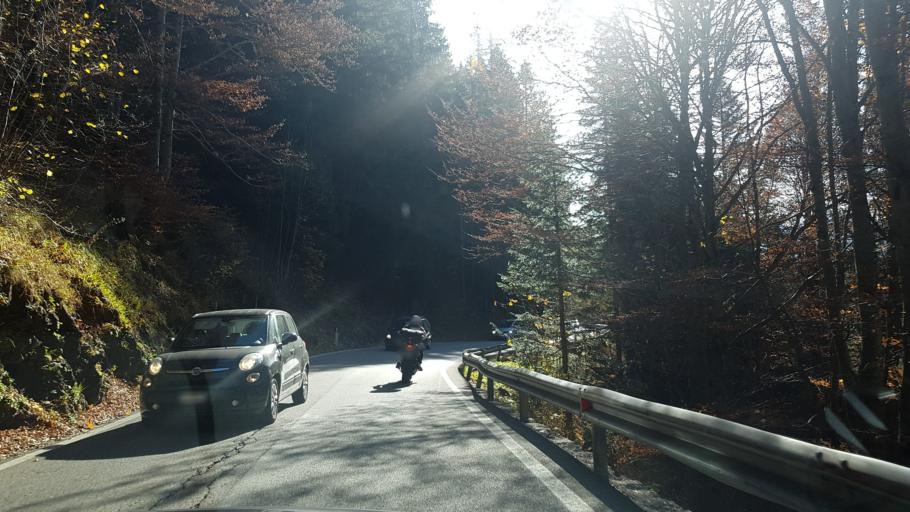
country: IT
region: Veneto
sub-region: Provincia di Belluno
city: Candide
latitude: 46.6437
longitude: 12.4538
